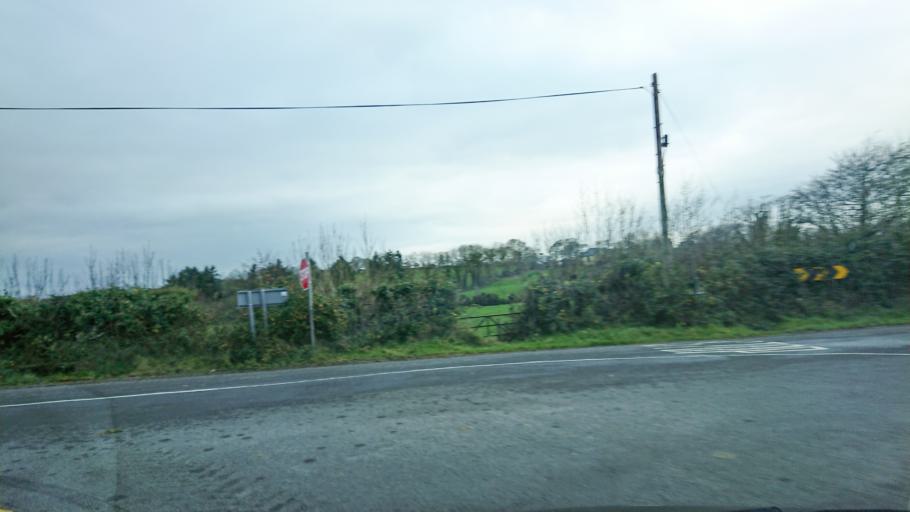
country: IE
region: Munster
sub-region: Waterford
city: Dunmore East
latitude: 52.2420
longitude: -7.0019
